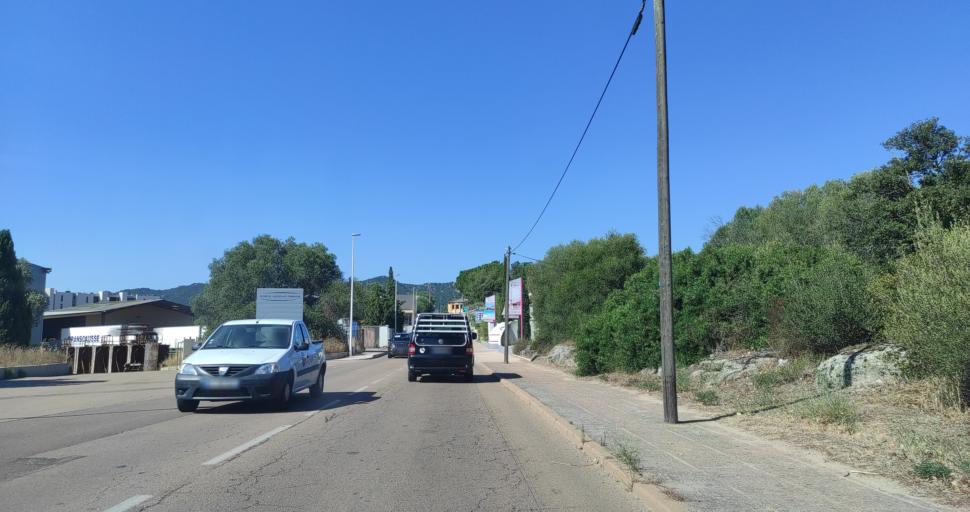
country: FR
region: Corsica
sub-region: Departement de la Corse-du-Sud
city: Porto-Vecchio
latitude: 41.5818
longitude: 9.2774
